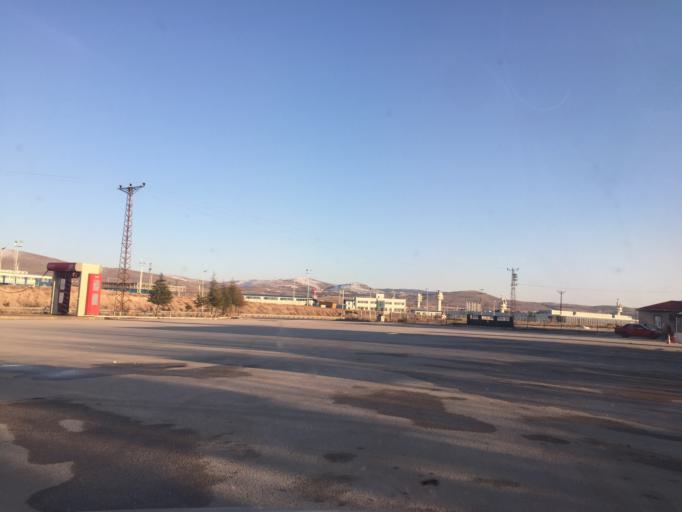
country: TR
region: Ankara
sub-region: Goelbasi
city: Golbasi
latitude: 39.7247
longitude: 32.8107
